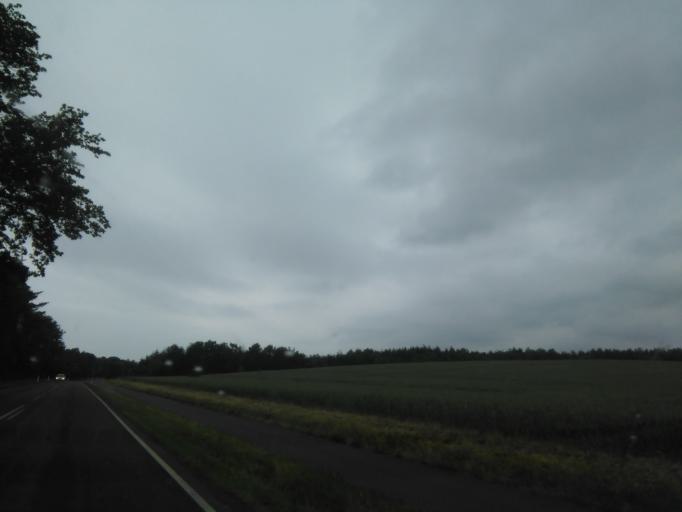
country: DK
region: Capital Region
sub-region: Bornholm Kommune
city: Akirkeby
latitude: 55.0508
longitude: 14.8123
